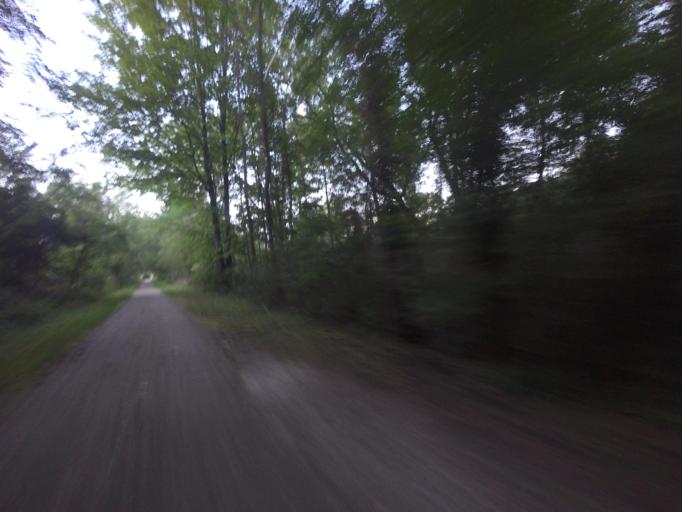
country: CA
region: Ontario
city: Orangeville
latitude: 43.9507
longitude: -79.8348
